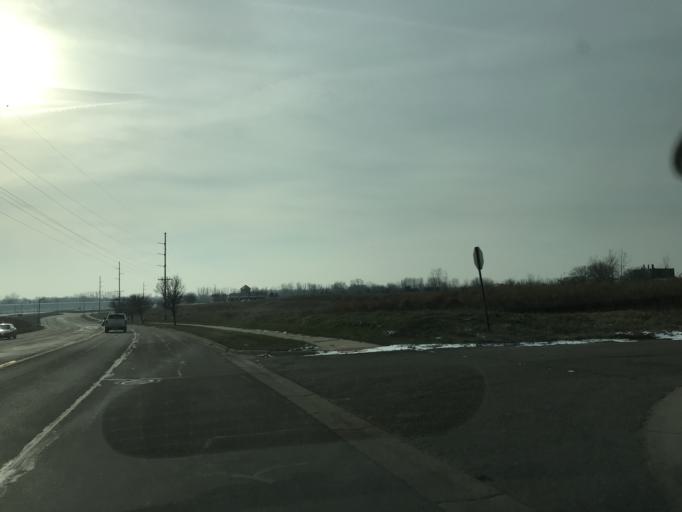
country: US
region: Michigan
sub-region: Ottawa County
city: Holland
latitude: 42.7536
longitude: -86.0771
